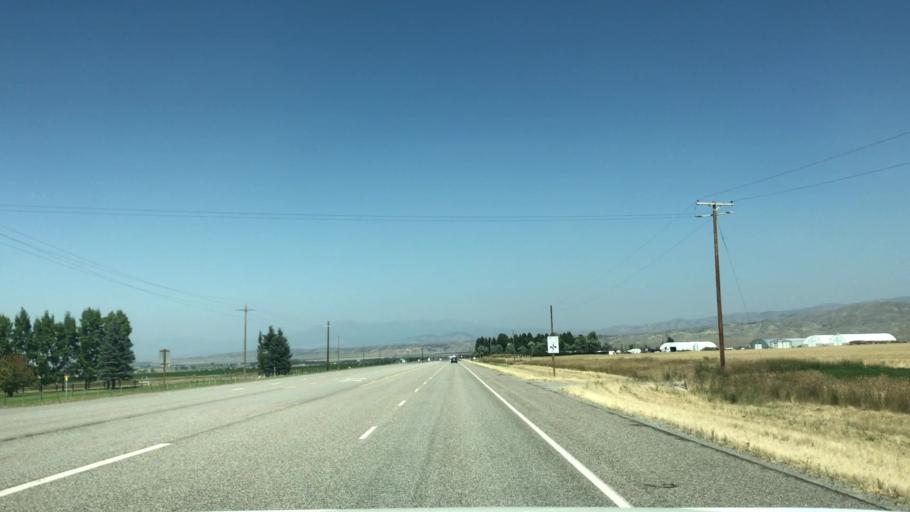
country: US
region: Montana
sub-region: Broadwater County
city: Townsend
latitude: 46.1367
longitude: -111.4814
